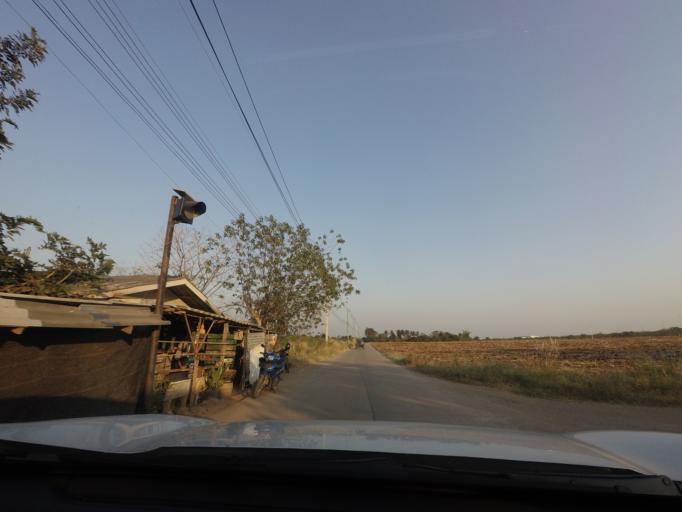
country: TH
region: Nakhon Ratchasima
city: Pak Chong
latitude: 14.6471
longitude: 101.3971
